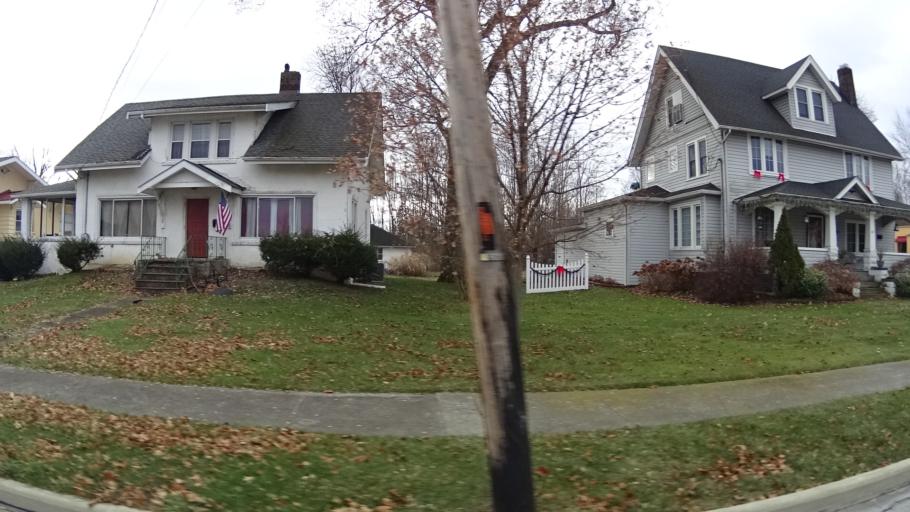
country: US
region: Ohio
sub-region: Lorain County
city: Wellington
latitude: 41.1685
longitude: -82.2084
